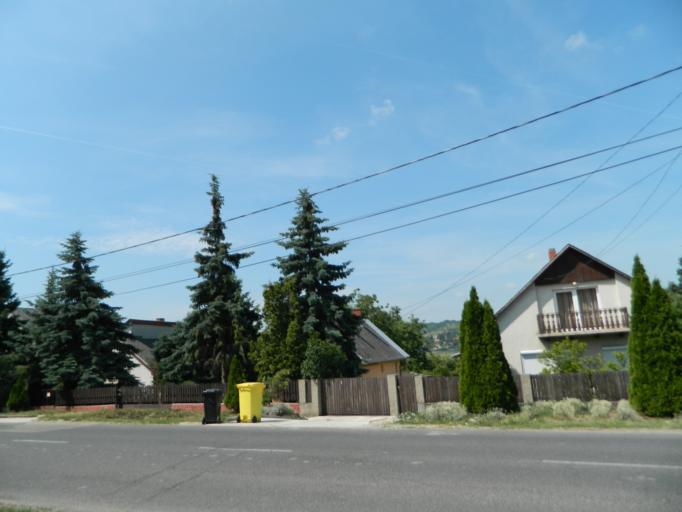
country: HU
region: Somogy
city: Balatonfoldvar
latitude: 46.8408
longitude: 17.8993
